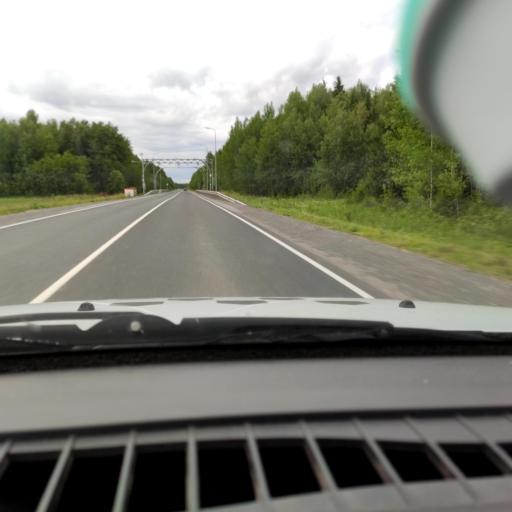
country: RU
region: Perm
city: Lys'va
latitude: 58.1767
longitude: 57.7858
